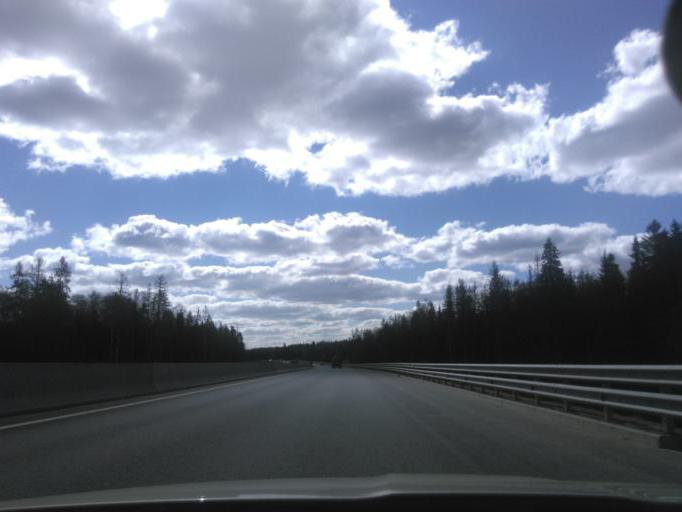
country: RU
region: Moskovskaya
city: Mendeleyevo
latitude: 56.0787
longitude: 37.2110
